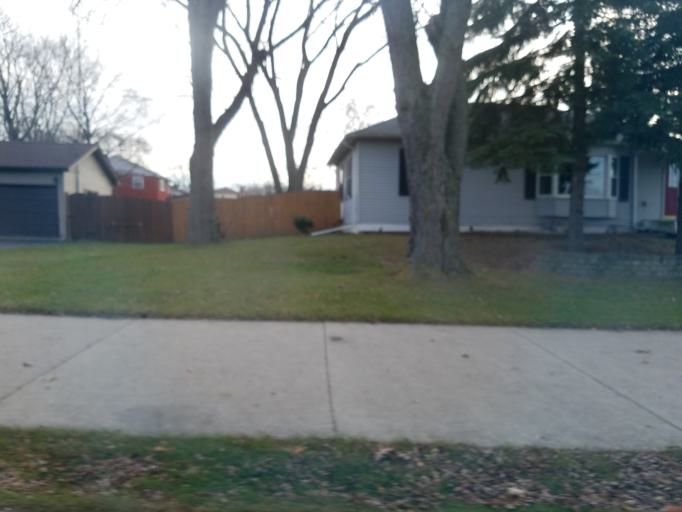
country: US
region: Illinois
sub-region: Will County
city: Mokena
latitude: 41.5265
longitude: -87.8881
